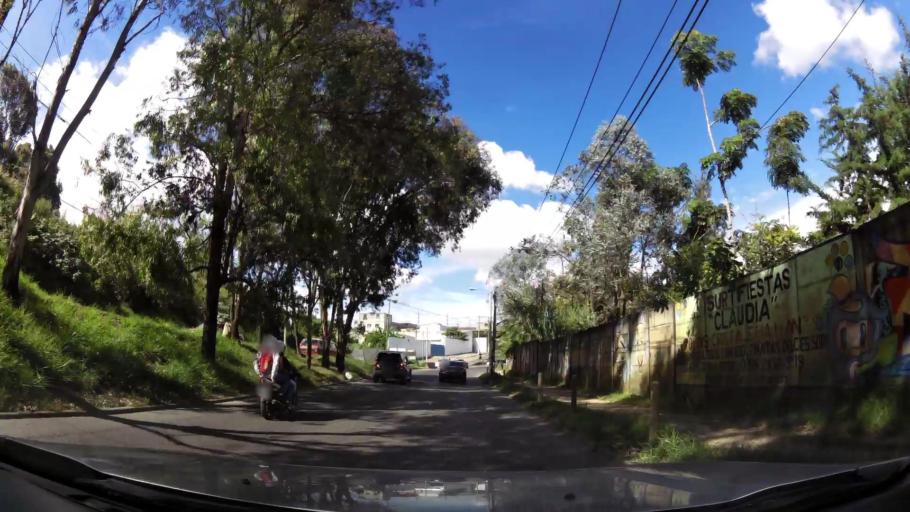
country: GT
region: Guatemala
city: Mixco
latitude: 14.6494
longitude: -90.5692
